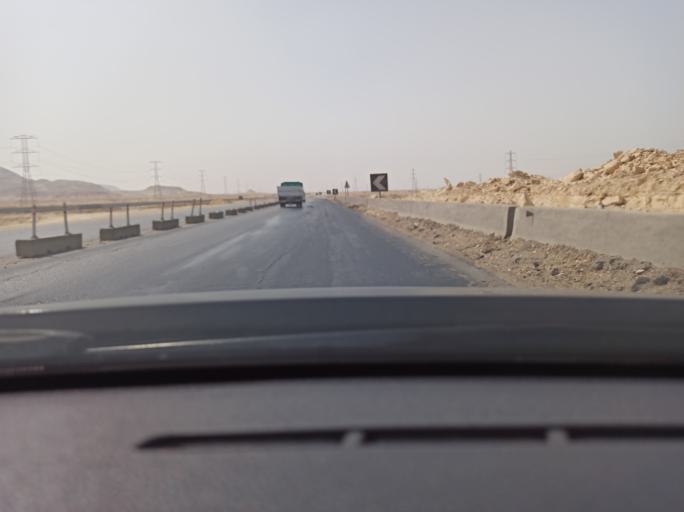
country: EG
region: Muhafazat Bani Suwayf
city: Bush
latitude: 29.1313
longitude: 31.2246
